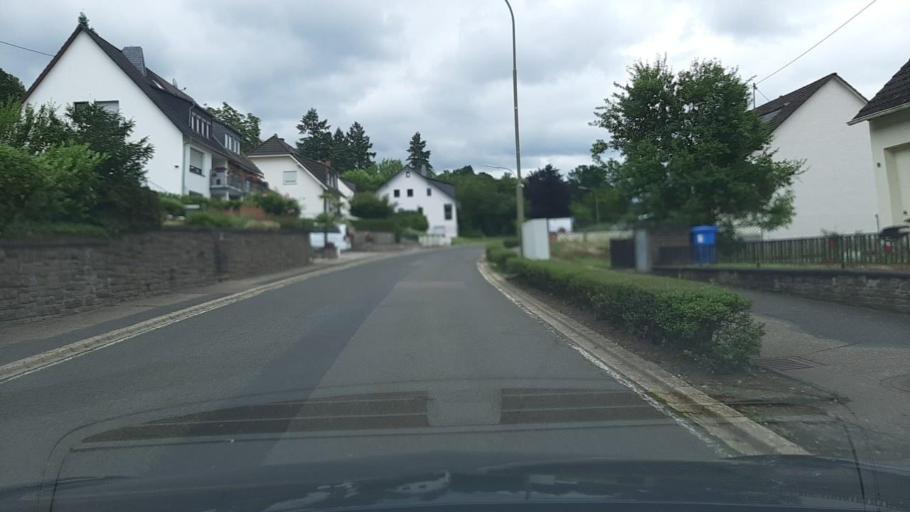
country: DE
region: Rheinland-Pfalz
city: Kamp-Bornhofen
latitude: 50.2216
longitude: 7.6022
